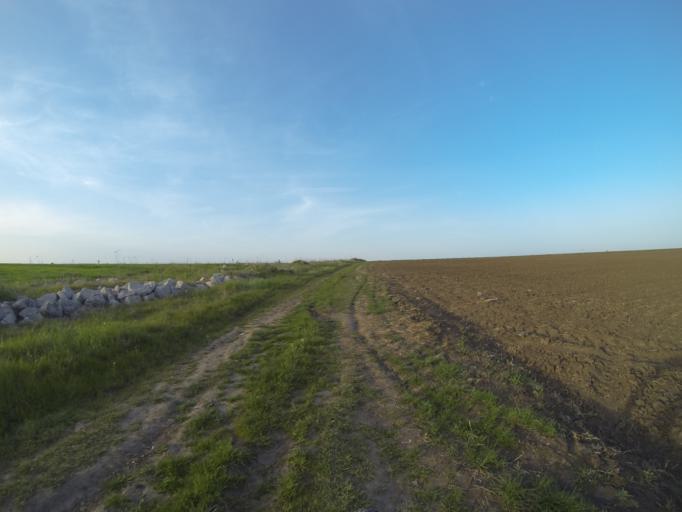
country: RO
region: Dolj
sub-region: Comuna Pielesti
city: Pielesti
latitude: 44.3329
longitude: 23.8954
